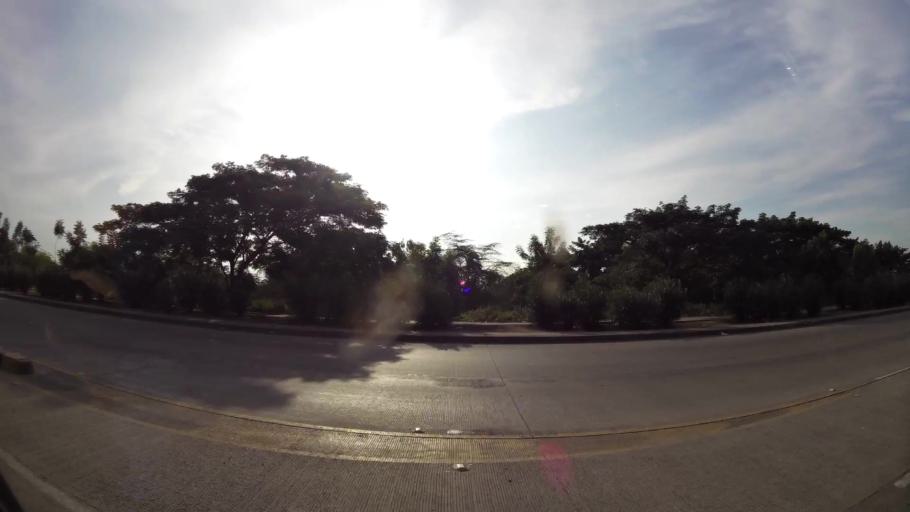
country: EC
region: Guayas
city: Eloy Alfaro
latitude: -2.0767
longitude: -79.8961
